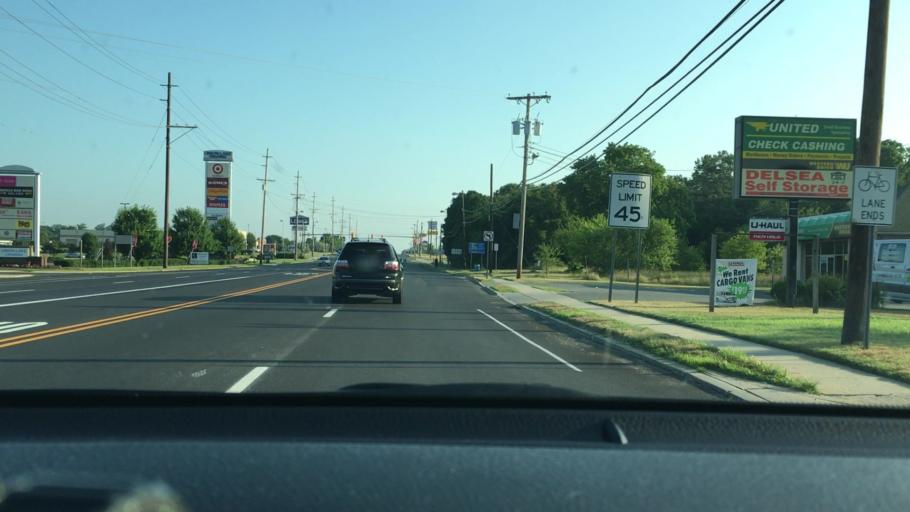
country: US
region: New Jersey
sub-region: Cumberland County
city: Millville
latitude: 39.4220
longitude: -75.0394
